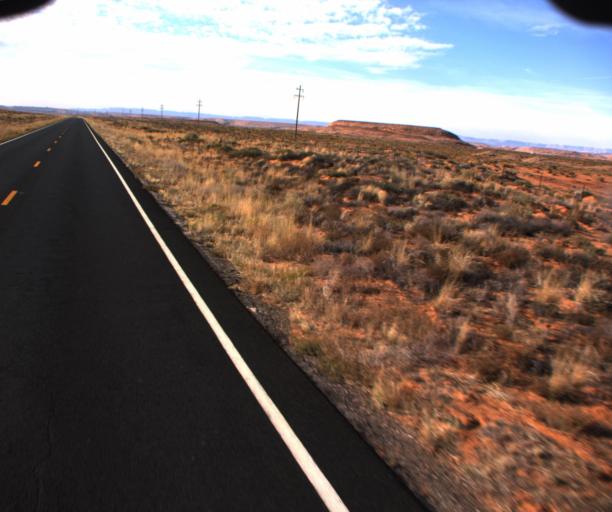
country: US
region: Arizona
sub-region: Apache County
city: Many Farms
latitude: 36.8458
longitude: -109.6400
